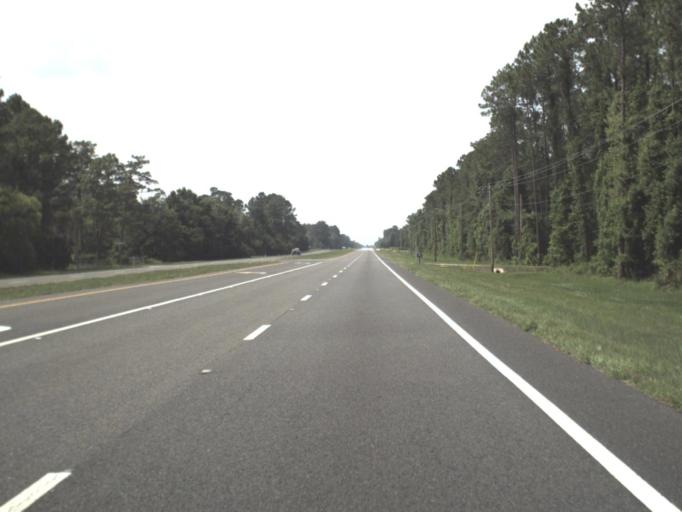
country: US
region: Florida
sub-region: Clay County
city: Green Cove Springs
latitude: 29.8957
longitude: -81.6712
